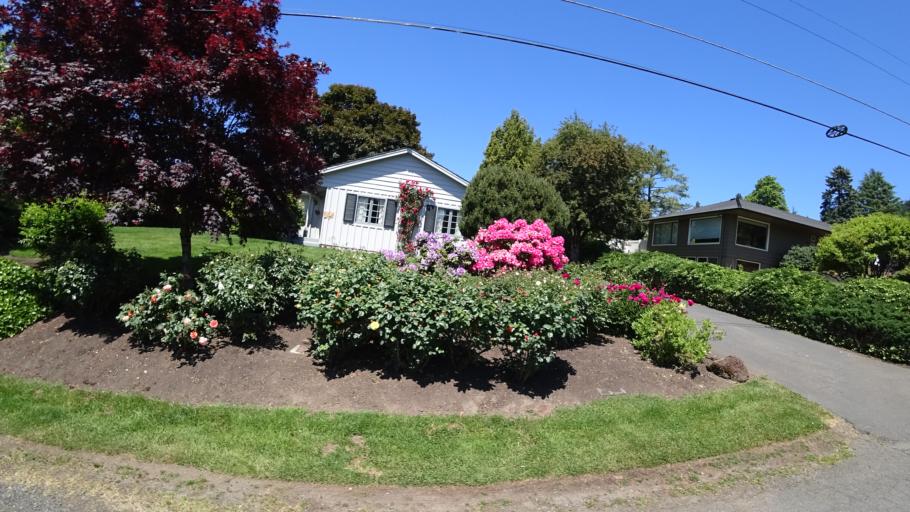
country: US
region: Oregon
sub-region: Washington County
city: Raleigh Hills
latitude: 45.4953
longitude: -122.7157
